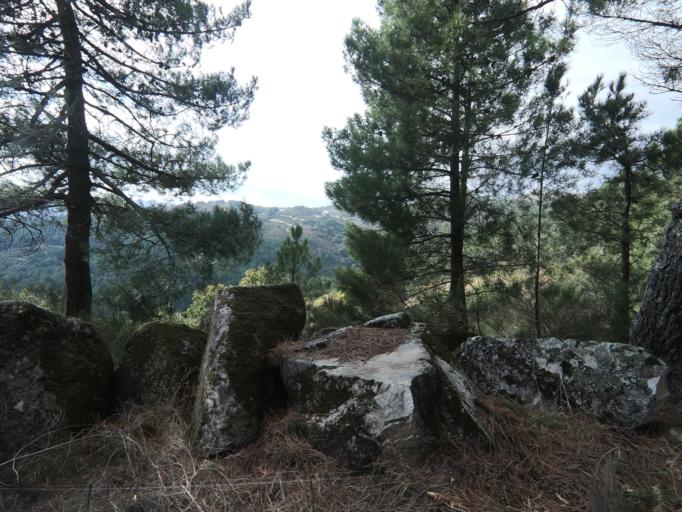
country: PT
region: Vila Real
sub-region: Vila Real
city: Vila Real
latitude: 41.3340
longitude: -7.7709
